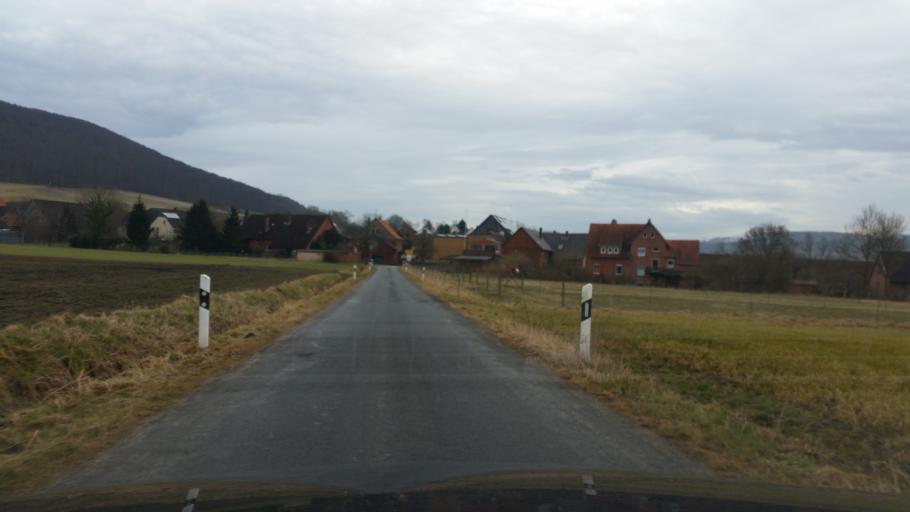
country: DE
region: Lower Saxony
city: Hameln
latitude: 52.1720
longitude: 9.3474
